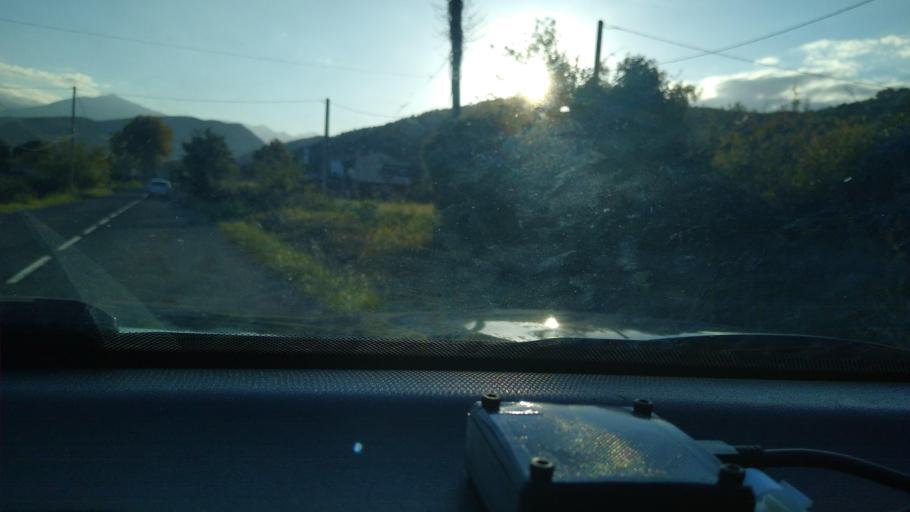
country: FR
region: Languedoc-Roussillon
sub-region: Departement des Pyrenees-Orientales
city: Prades
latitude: 42.6285
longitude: 2.4218
